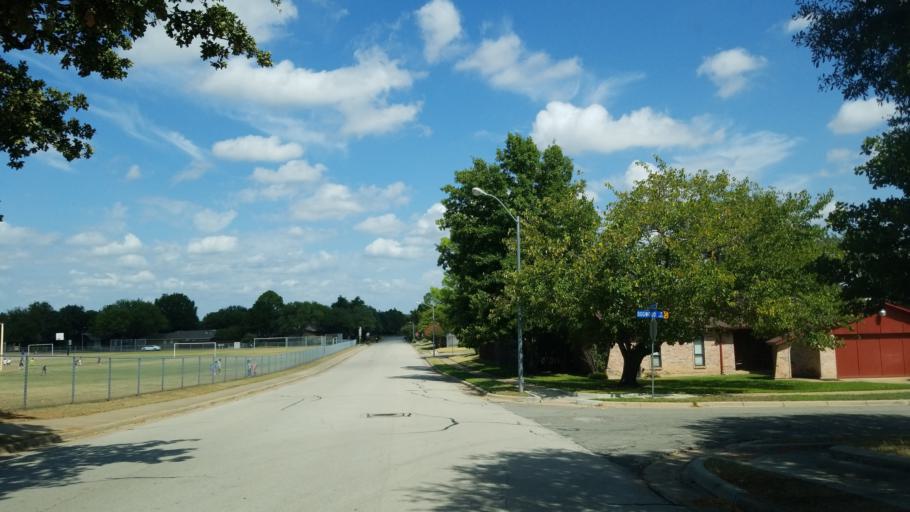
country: US
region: Texas
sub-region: Tarrant County
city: Euless
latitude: 32.8594
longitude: -97.0928
